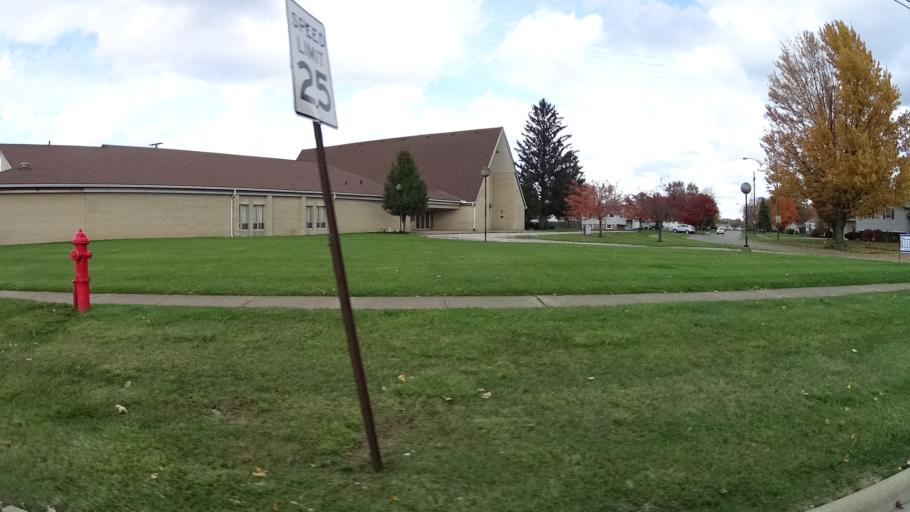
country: US
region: Ohio
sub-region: Lorain County
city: Lorain
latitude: 41.4417
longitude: -82.2008
